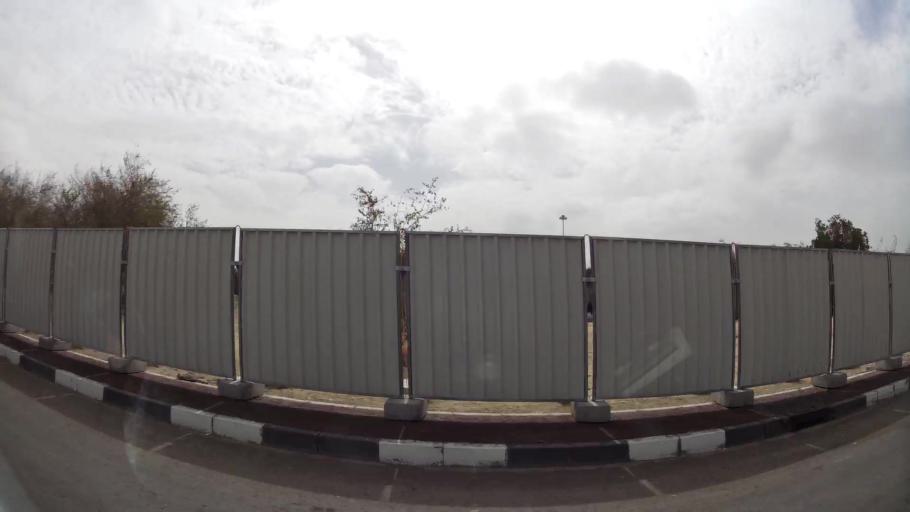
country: AE
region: Abu Dhabi
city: Abu Dhabi
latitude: 24.3953
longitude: 54.5183
